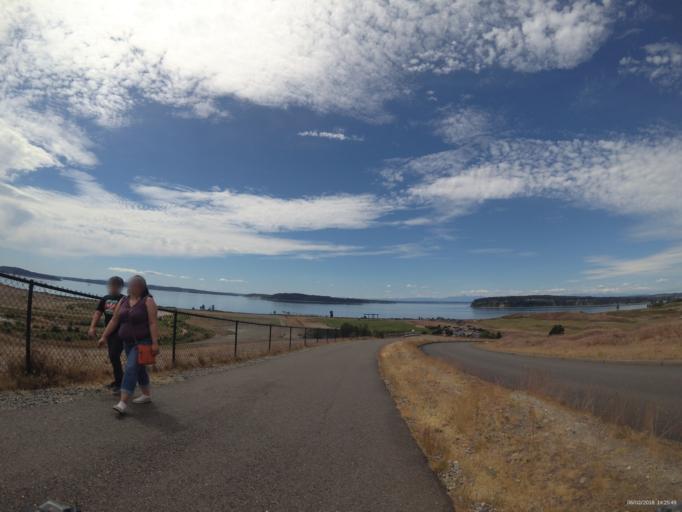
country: US
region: Washington
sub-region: Pierce County
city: University Place
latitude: 47.1996
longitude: -122.5724
